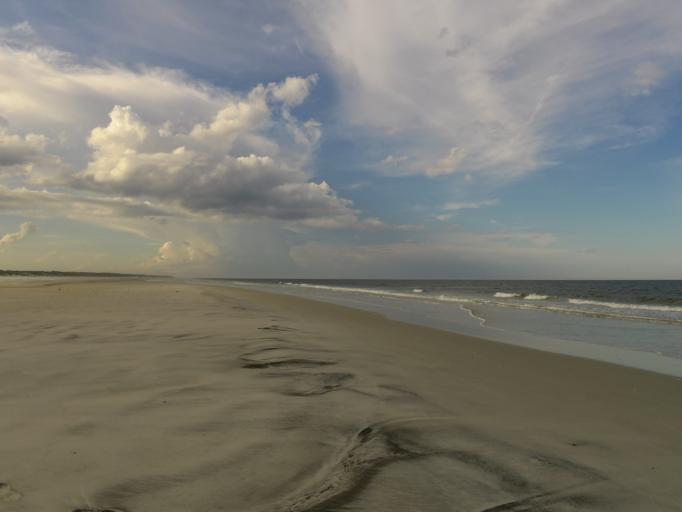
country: US
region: Florida
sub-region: Duval County
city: Atlantic Beach
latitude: 30.4434
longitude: -81.4086
